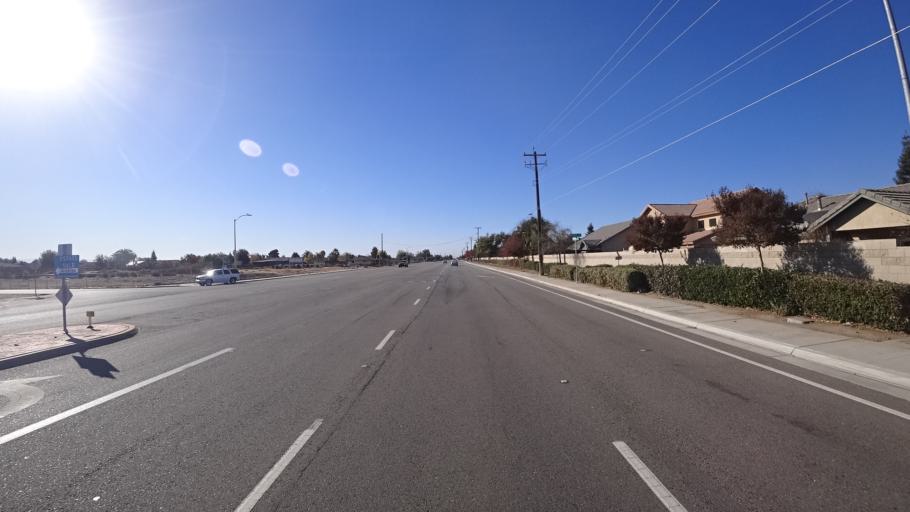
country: US
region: California
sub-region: Kern County
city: Greenfield
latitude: 35.2814
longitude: -119.0309
